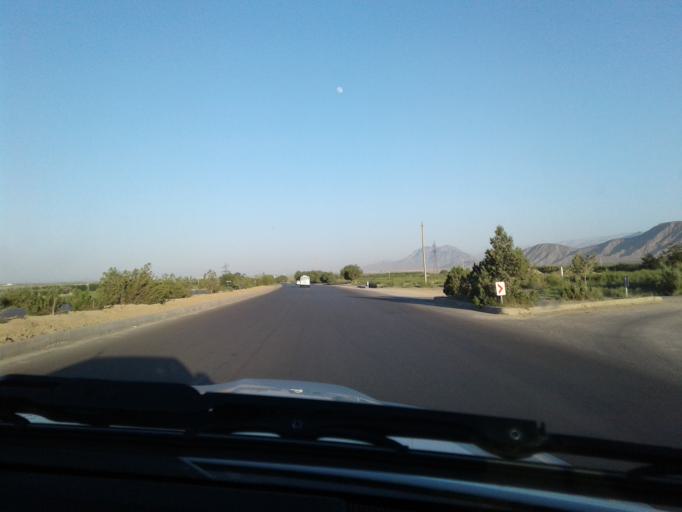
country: TM
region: Ahal
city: Arcabil
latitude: 38.1967
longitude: 57.8312
